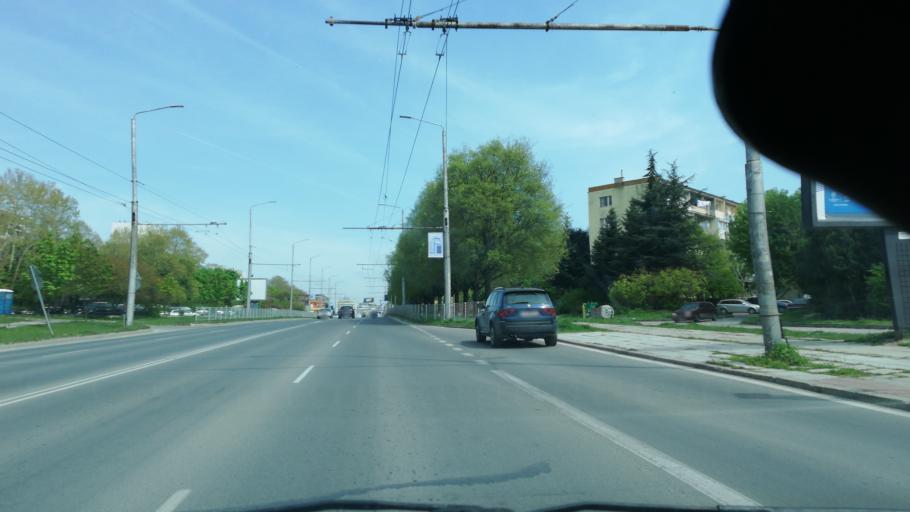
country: BG
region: Varna
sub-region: Obshtina Varna
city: Varna
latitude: 43.2276
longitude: 27.8805
